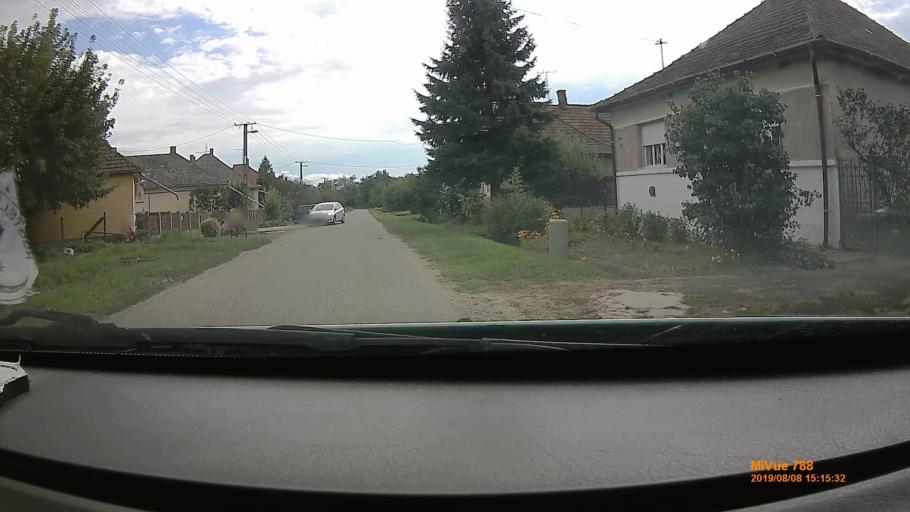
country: HU
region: Szabolcs-Szatmar-Bereg
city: Tunyogmatolcs
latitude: 47.9681
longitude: 22.4579
